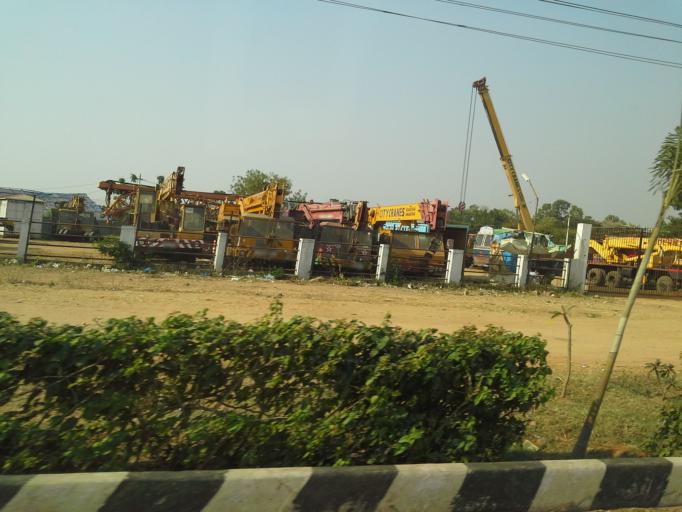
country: IN
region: Telangana
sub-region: Rangareddi
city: Balapur
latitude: 17.2731
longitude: 78.3989
